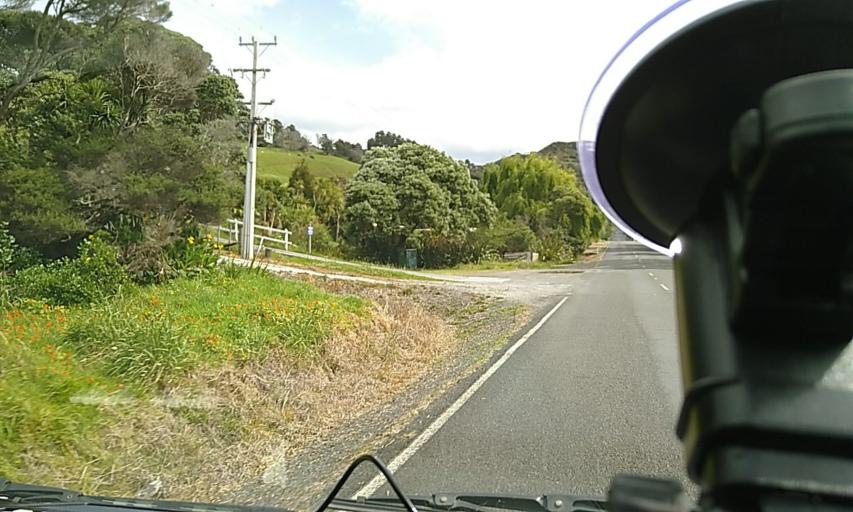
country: NZ
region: Northland
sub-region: Far North District
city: Ahipara
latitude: -35.5328
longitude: 173.3892
